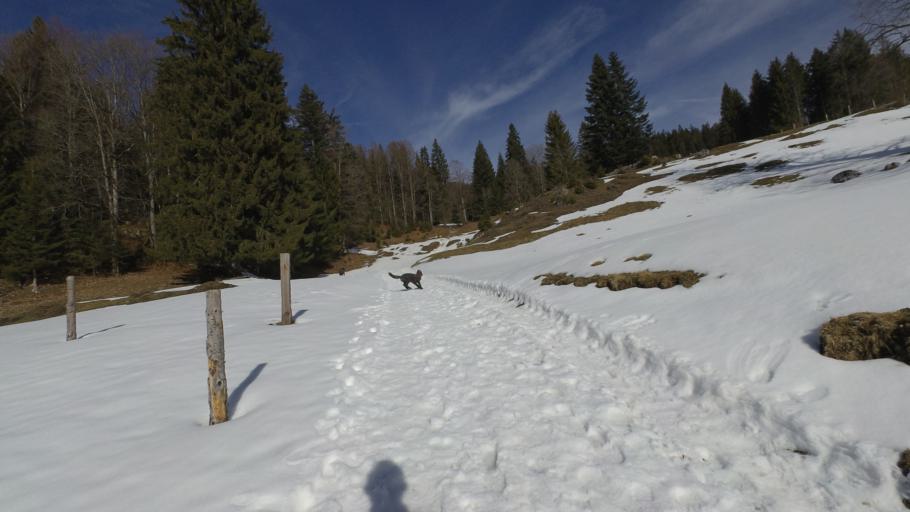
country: DE
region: Bavaria
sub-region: Upper Bavaria
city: Reit im Winkl
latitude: 47.6855
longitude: 12.4447
